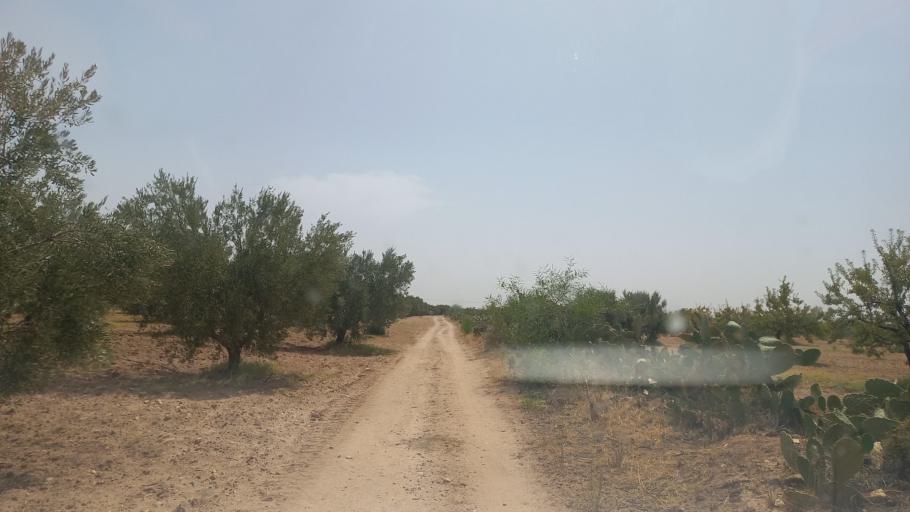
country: TN
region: Al Qasrayn
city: Kasserine
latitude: 35.2596
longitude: 9.0055
